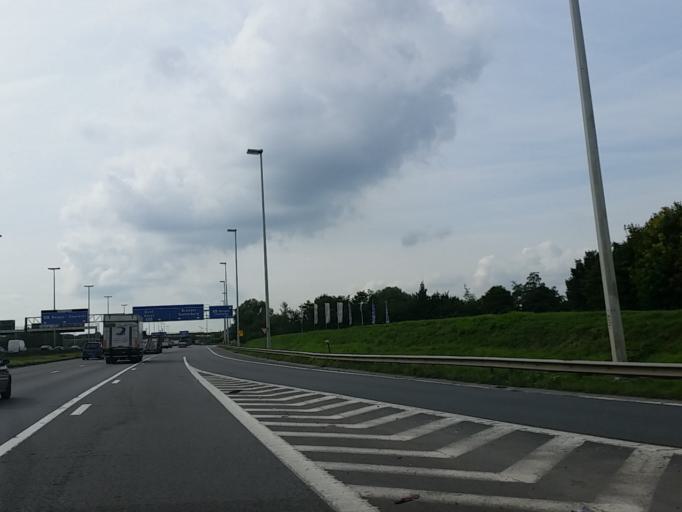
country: BE
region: Flanders
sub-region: Provincie Vlaams-Brabant
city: Wemmel
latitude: 50.8814
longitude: 4.2829
